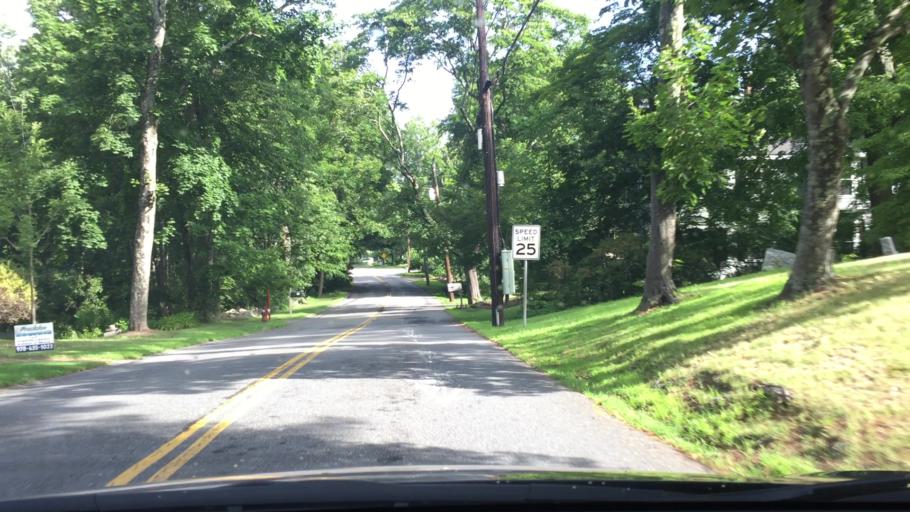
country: US
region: Massachusetts
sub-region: Middlesex County
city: Acton
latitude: 42.4879
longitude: -71.4315
